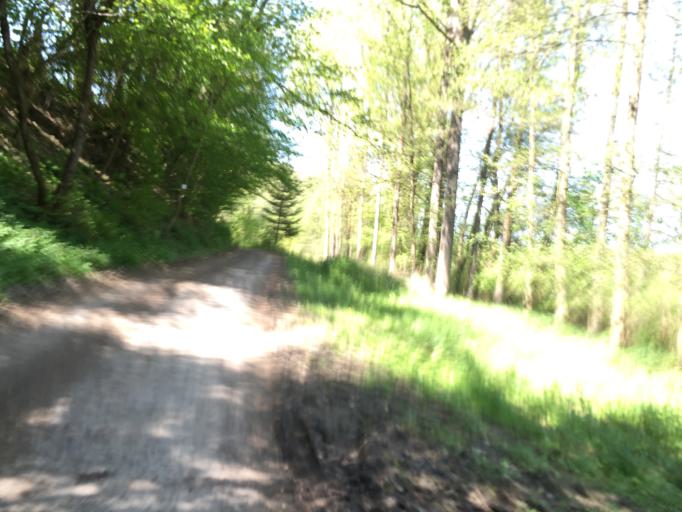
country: DE
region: Bavaria
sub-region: Regierungsbezirk Unterfranken
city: Hosbach
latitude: 50.0119
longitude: 9.1977
